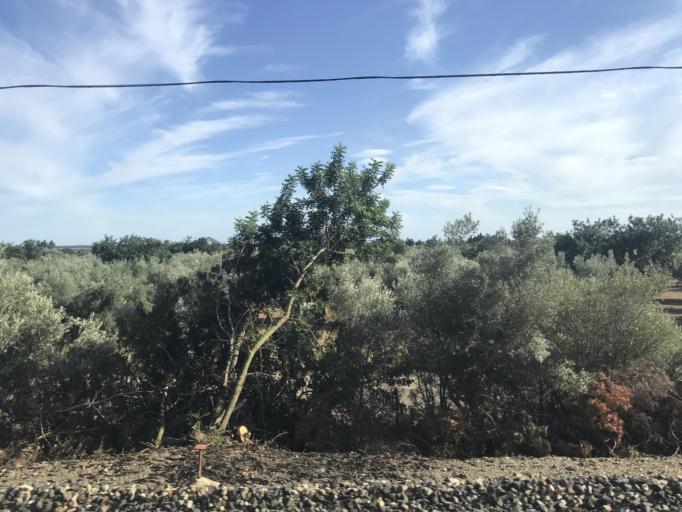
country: ES
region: Catalonia
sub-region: Provincia de Tarragona
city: Camarles
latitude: 40.7567
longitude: 0.6221
